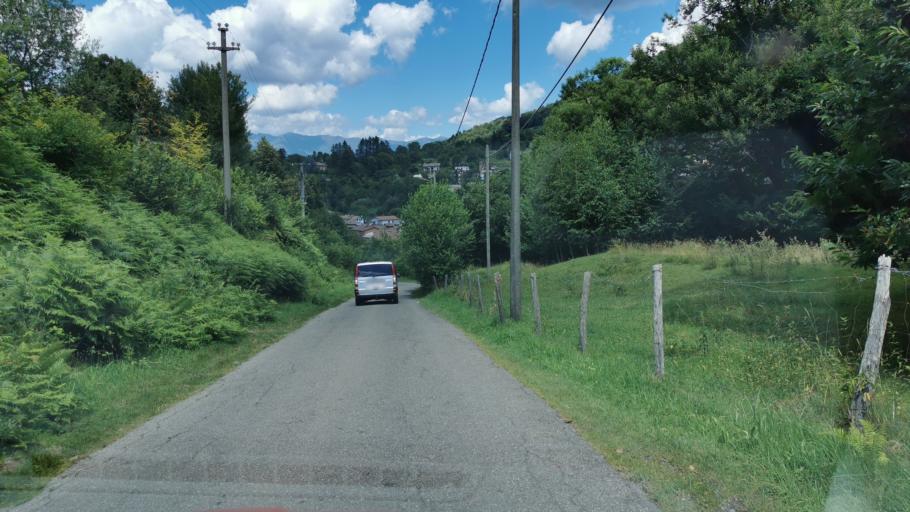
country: IT
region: Lombardy
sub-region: Provincia di Como
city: San Fedele Superiore
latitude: 45.9682
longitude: 9.0676
